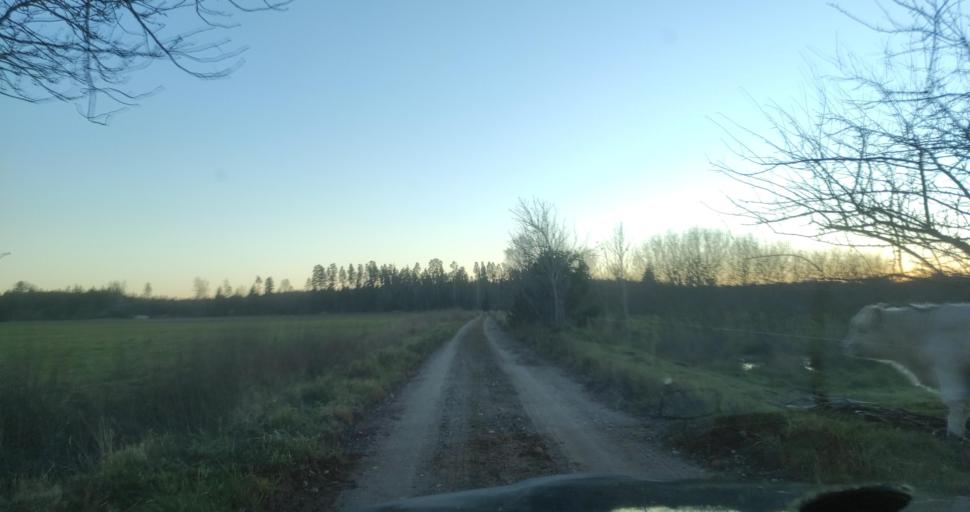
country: LV
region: Dundaga
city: Dundaga
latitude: 57.3732
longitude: 22.2259
